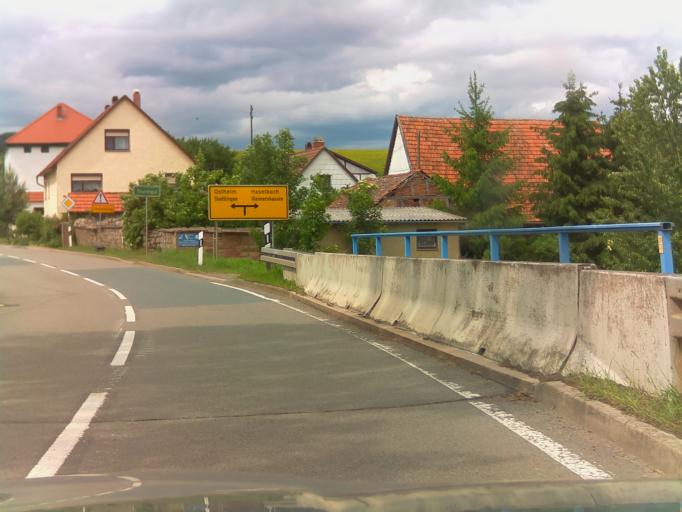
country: DE
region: Thuringia
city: Henneberg
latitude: 50.5116
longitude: 10.3192
